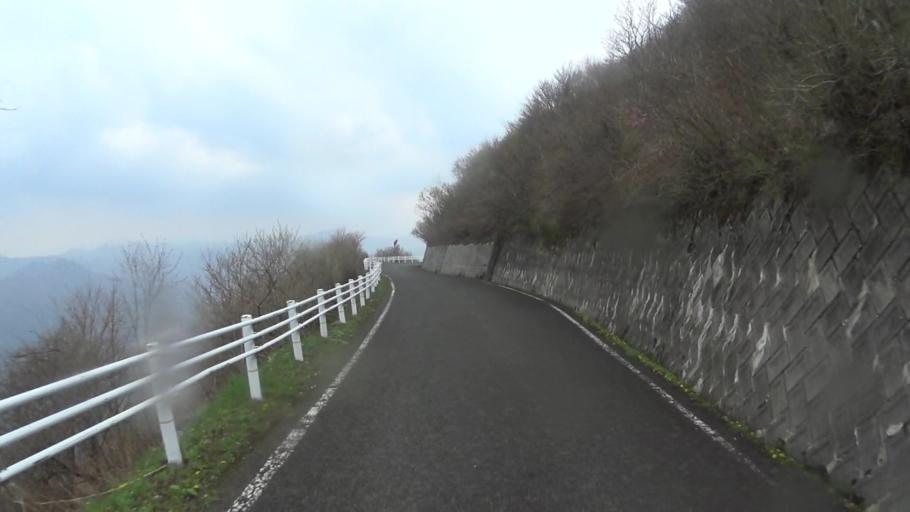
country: JP
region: Ehime
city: Saijo
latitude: 33.7805
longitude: 133.2243
